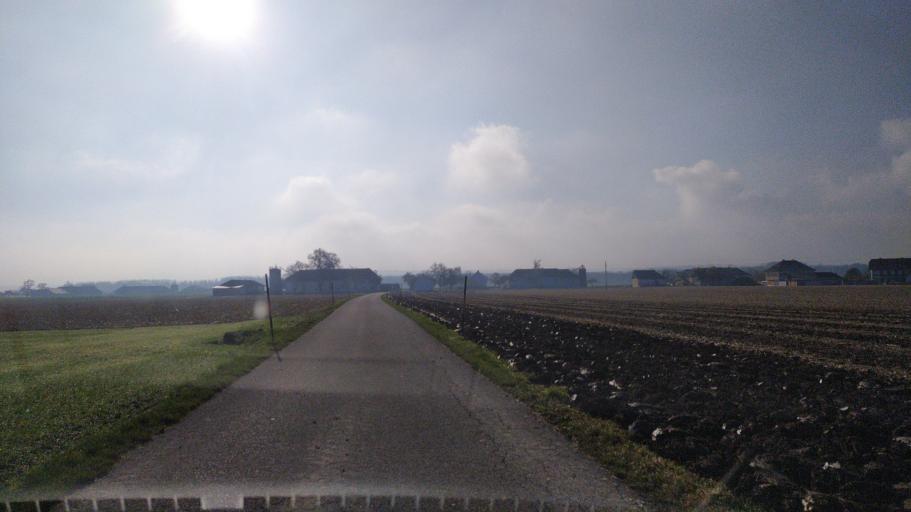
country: AT
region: Lower Austria
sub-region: Politischer Bezirk Amstetten
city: Strengberg
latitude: 48.1916
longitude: 14.6549
